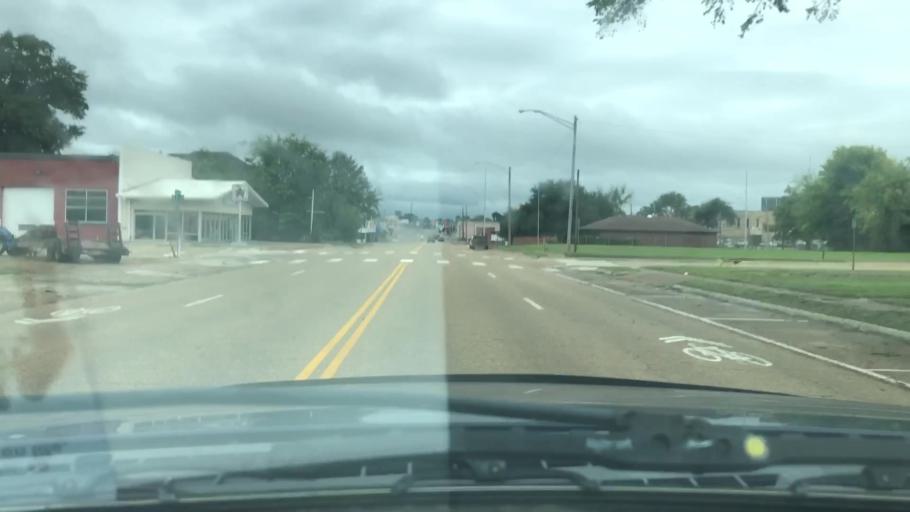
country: US
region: Texas
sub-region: Bowie County
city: Texarkana
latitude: 33.4229
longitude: -94.0466
